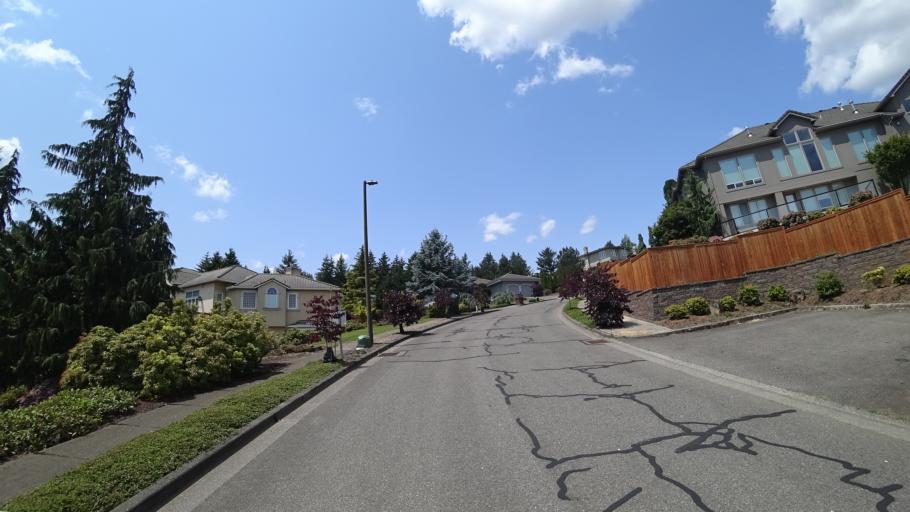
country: US
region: Oregon
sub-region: Clackamas County
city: Happy Valley
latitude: 45.4459
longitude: -122.5420
